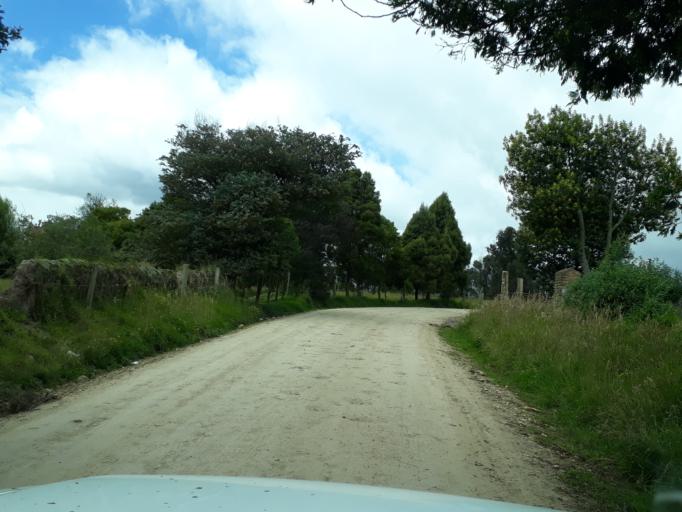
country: CO
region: Cundinamarca
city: Guasca
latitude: 4.8490
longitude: -73.9089
